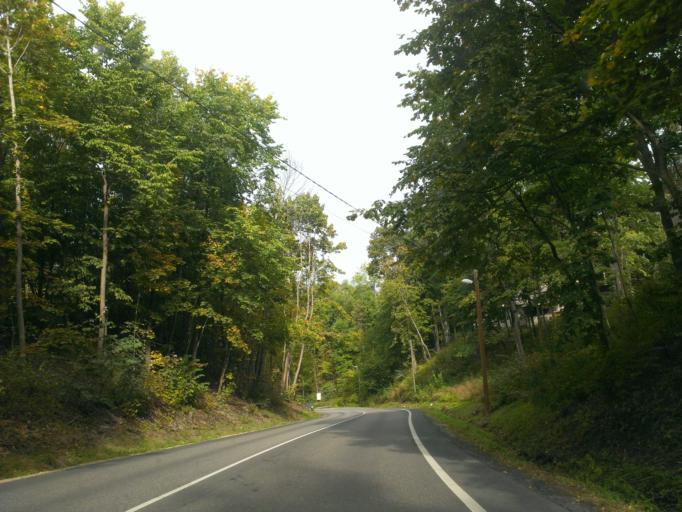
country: LV
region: Sigulda
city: Sigulda
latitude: 57.1626
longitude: 24.8504
